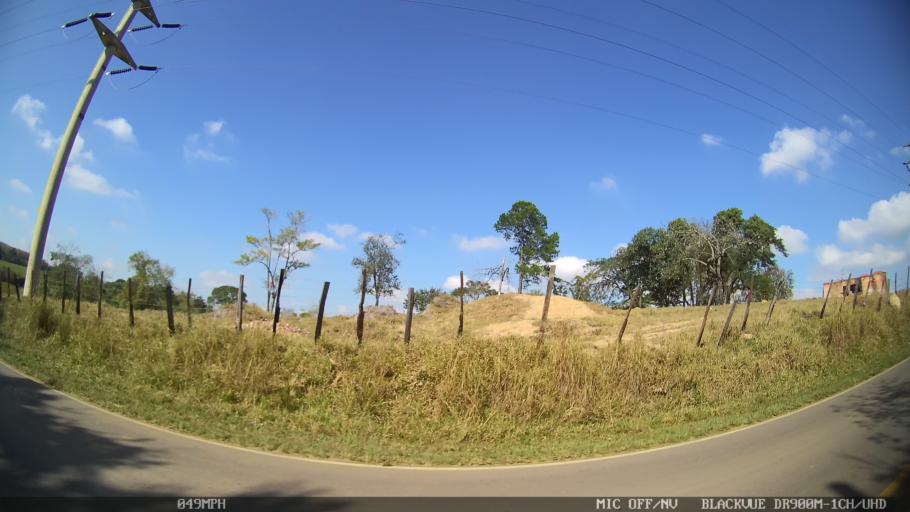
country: BR
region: Sao Paulo
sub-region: Indaiatuba
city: Indaiatuba
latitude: -22.9938
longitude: -47.1795
